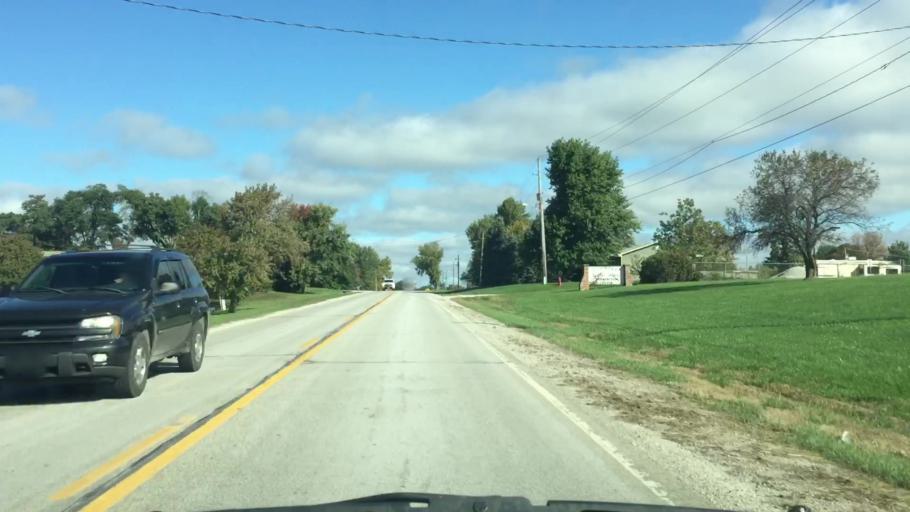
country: US
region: Iowa
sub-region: Decatur County
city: Leon
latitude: 40.7336
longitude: -93.7612
